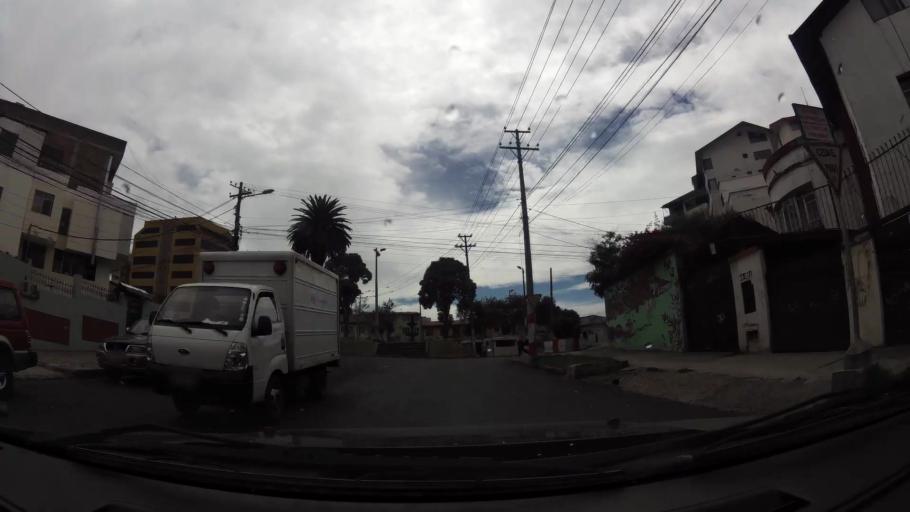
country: EC
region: Pichincha
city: Quito
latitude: -0.2114
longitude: -78.4829
